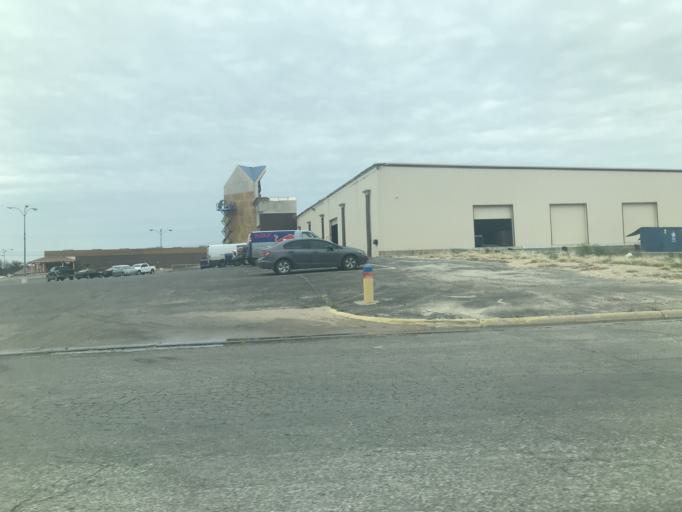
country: US
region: Texas
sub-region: Tom Green County
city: San Angelo
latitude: 31.4207
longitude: -100.4753
